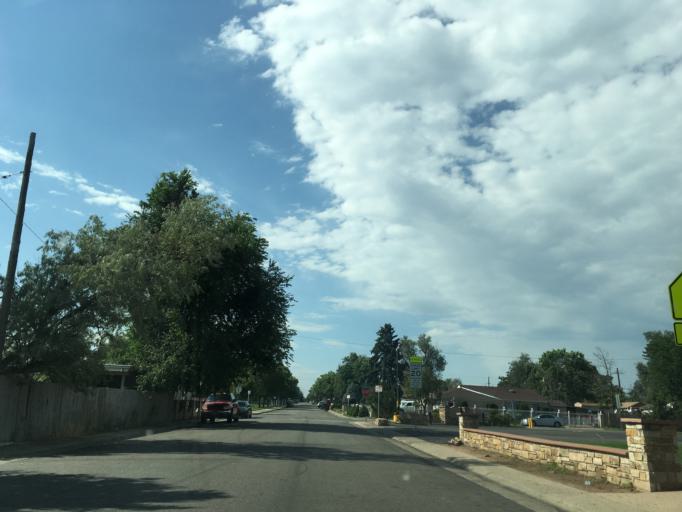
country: US
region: Colorado
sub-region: Jefferson County
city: Lakewood
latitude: 39.7028
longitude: -105.0368
